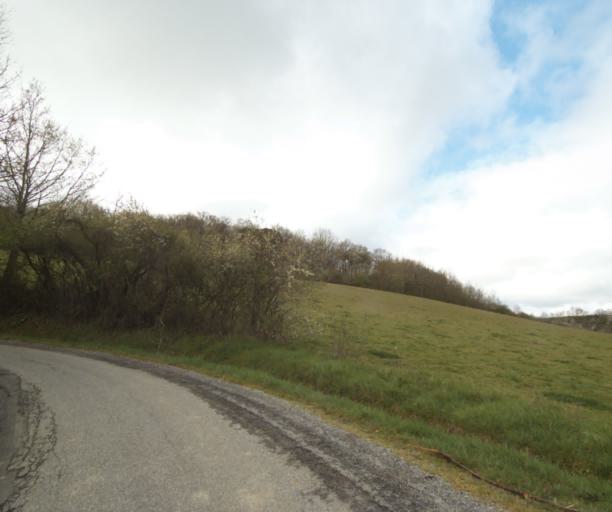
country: FR
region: Midi-Pyrenees
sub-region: Departement de l'Ariege
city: Saverdun
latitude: 43.2243
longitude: 1.5451
